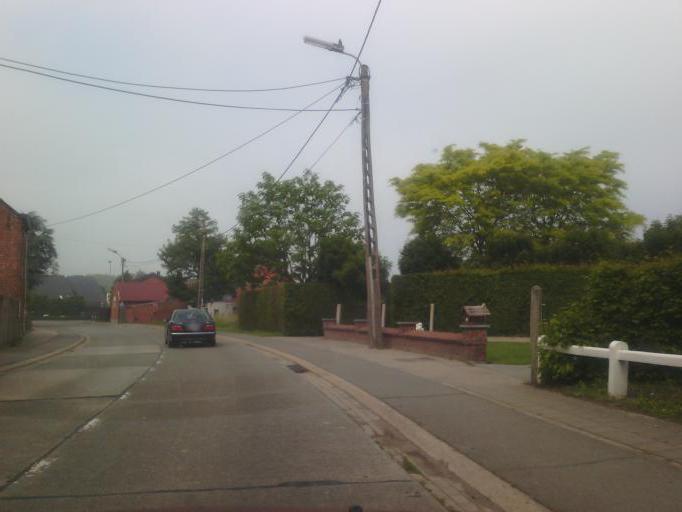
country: BE
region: Flanders
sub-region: Provincie Oost-Vlaanderen
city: Berlare
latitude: 50.9962
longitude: 4.0247
